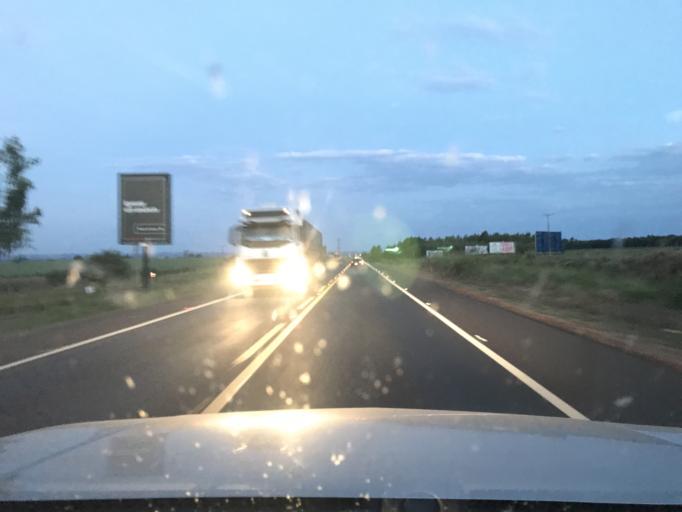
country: PY
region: Canindeyu
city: Salto del Guaira
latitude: -24.0153
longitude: -54.2991
